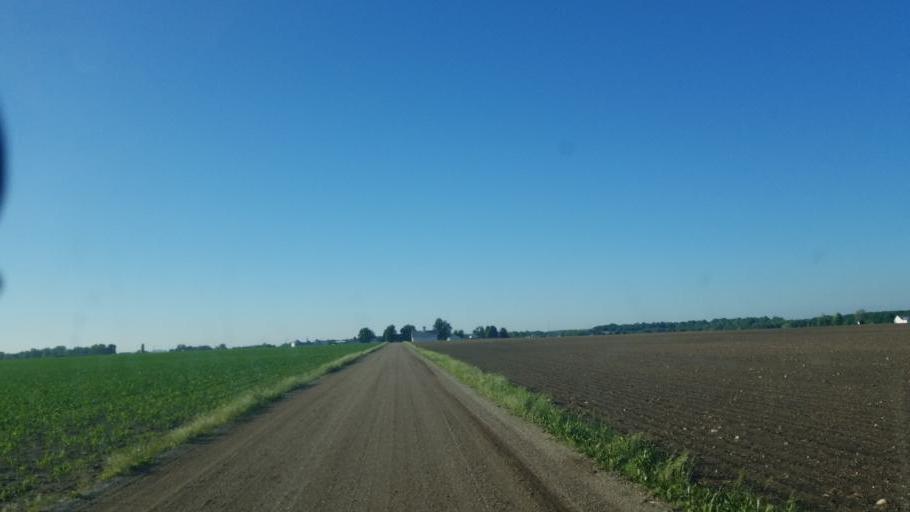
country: US
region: Indiana
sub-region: Marshall County
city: Bremen
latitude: 41.4193
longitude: -86.0975
